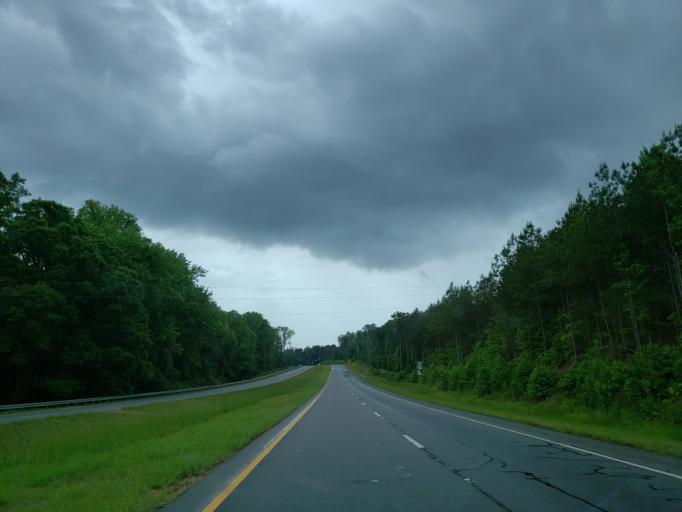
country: US
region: Georgia
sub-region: Haralson County
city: Buchanan
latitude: 33.8370
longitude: -85.2094
